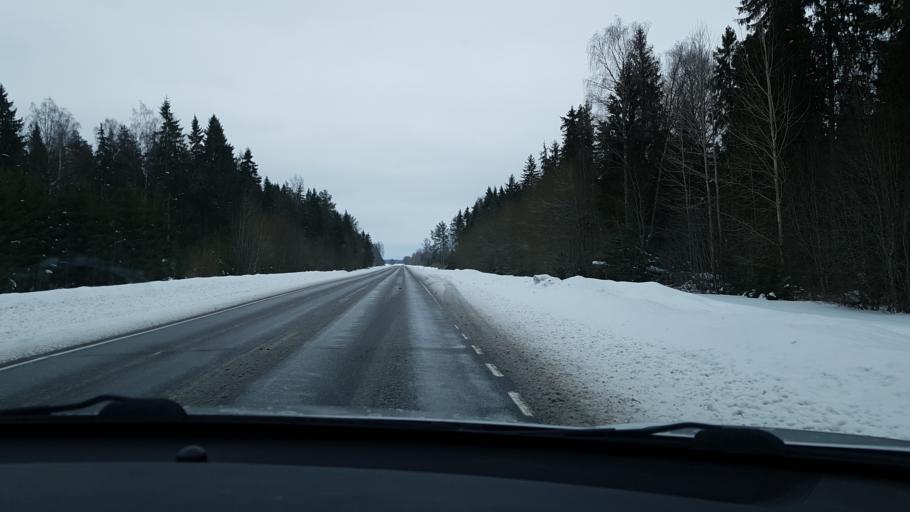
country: EE
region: Jaervamaa
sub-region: Jaerva-Jaani vald
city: Jarva-Jaani
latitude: 59.1330
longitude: 25.7767
